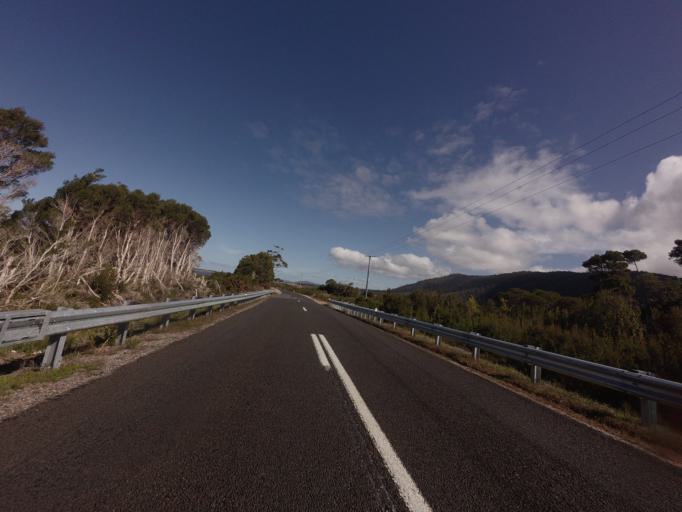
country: AU
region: Tasmania
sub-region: Break O'Day
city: St Helens
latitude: -41.7132
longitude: 148.2745
